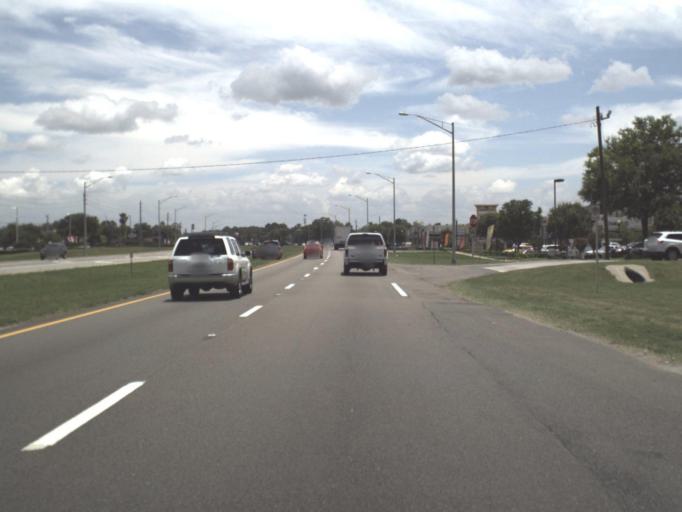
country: US
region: Florida
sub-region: Duval County
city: Jacksonville
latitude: 30.2693
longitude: -81.5590
